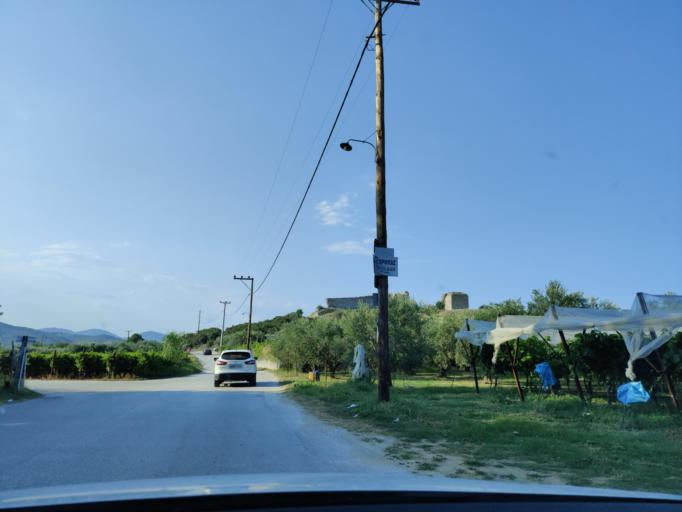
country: GR
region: East Macedonia and Thrace
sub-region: Nomos Kavalas
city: Nea Peramos
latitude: 40.8223
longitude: 24.3078
